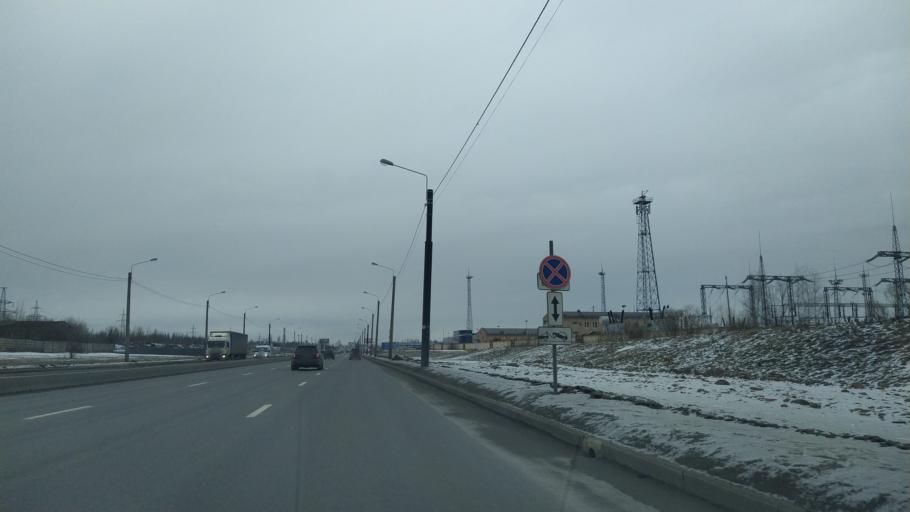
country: RU
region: St.-Petersburg
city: Krasnogvargeisky
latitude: 59.9715
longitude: 30.4578
